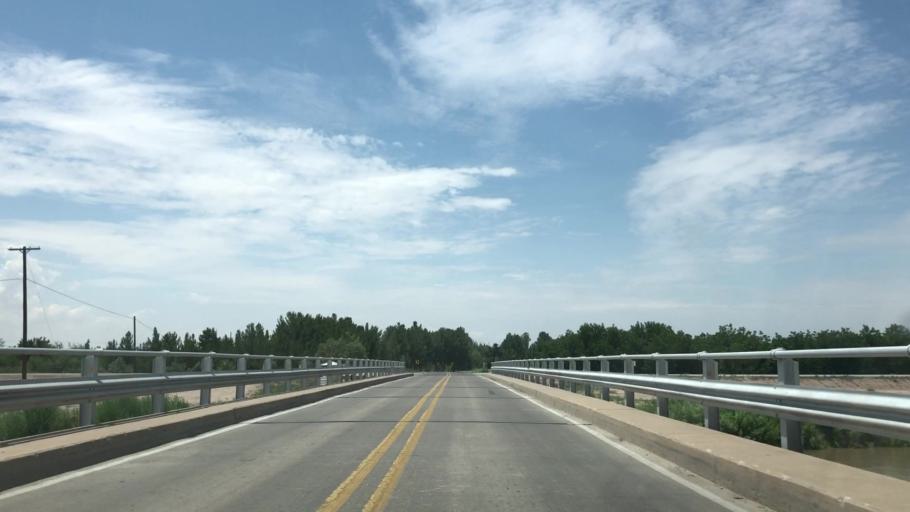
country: US
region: New Mexico
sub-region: Dona Ana County
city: Vado
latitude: 32.1135
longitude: -106.6689
